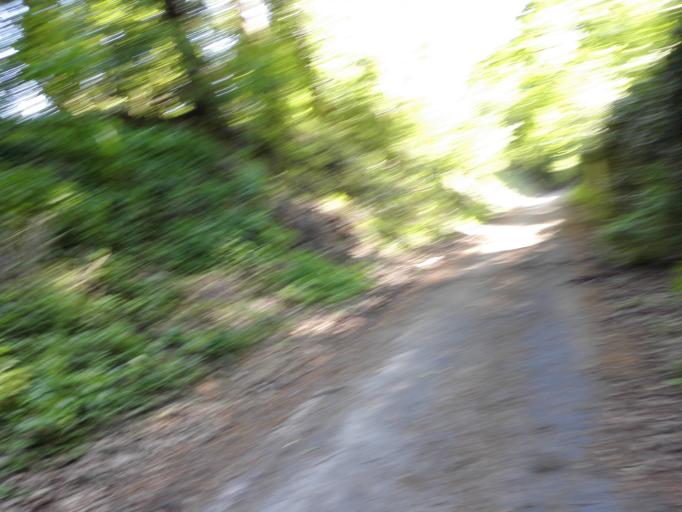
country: BE
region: Flanders
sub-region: Provincie Vlaams-Brabant
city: Tervuren
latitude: 50.8279
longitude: 4.5422
